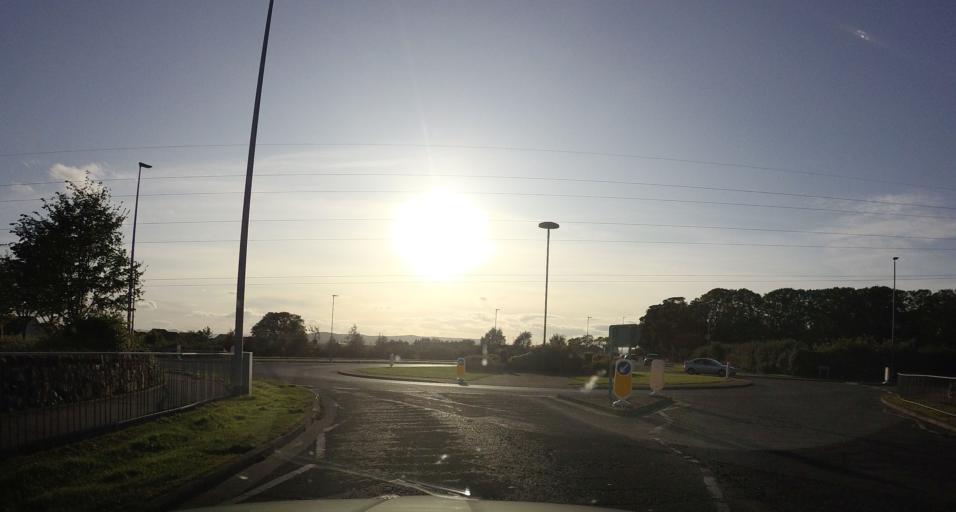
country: GB
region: Scotland
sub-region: Aberdeenshire
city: Westhill
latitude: 57.1520
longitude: -2.3100
